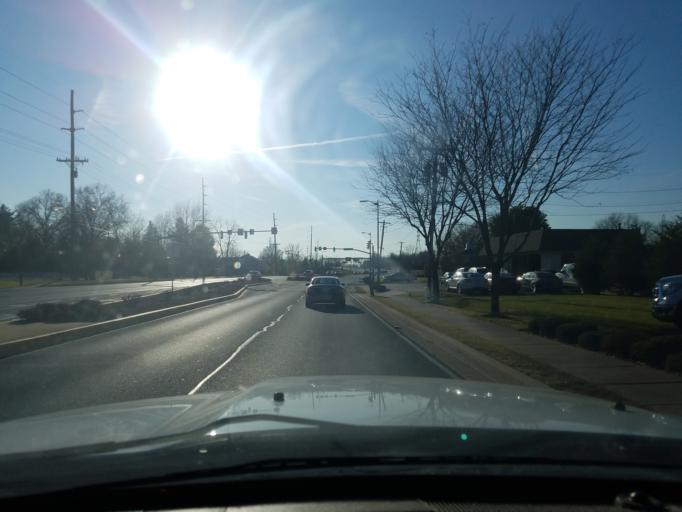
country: US
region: Indiana
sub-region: Clark County
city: Clarksville
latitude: 38.3061
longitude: -85.7765
